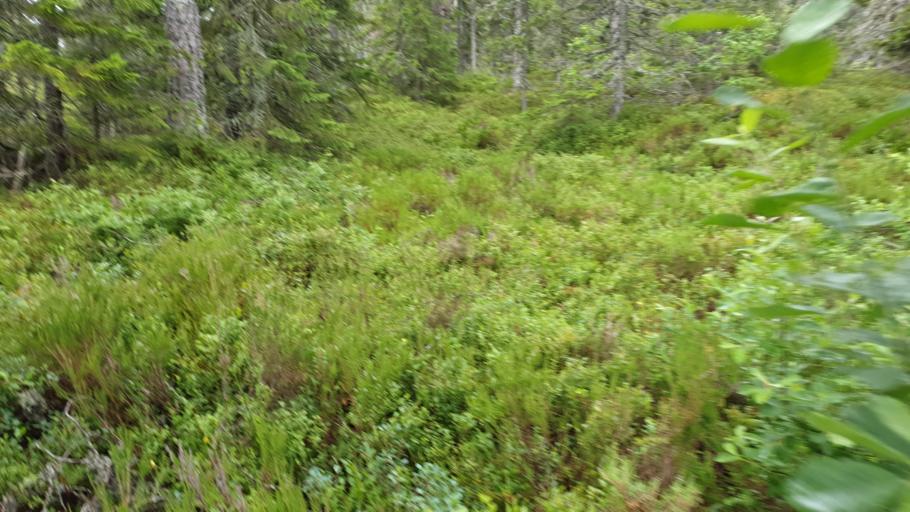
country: SE
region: Gaevleborg
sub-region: Hudiksvalls Kommun
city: Sorforsa
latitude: 61.6453
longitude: 16.7649
